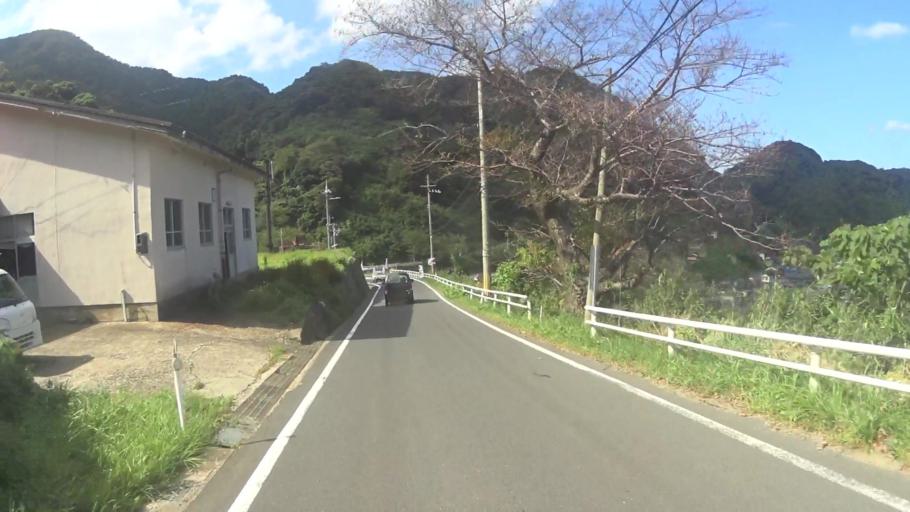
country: JP
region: Kyoto
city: Miyazu
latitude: 35.7503
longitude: 135.2508
